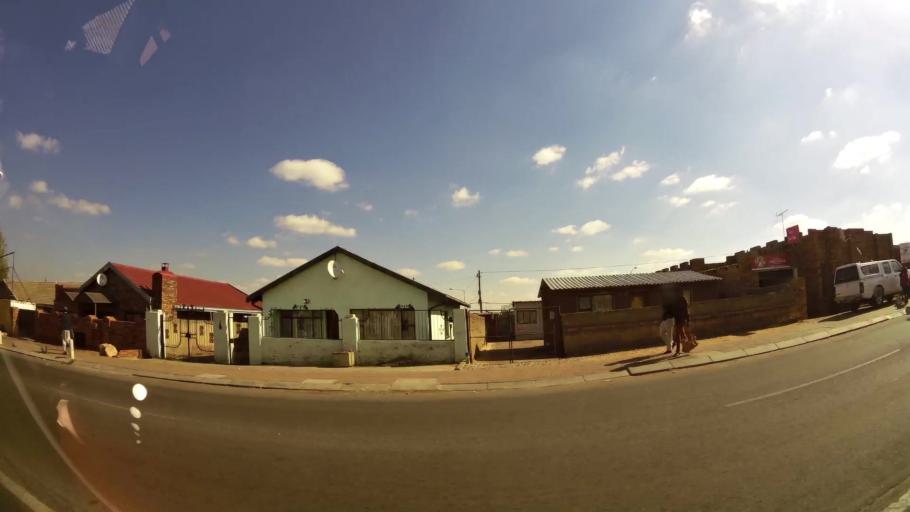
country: ZA
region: Gauteng
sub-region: West Rand District Municipality
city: Krugersdorp
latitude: -26.1630
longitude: 27.7804
